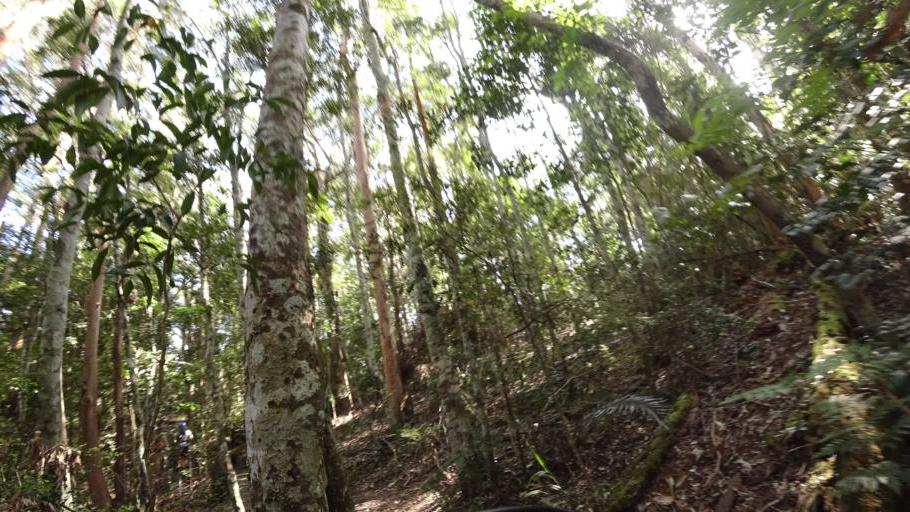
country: AU
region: Queensland
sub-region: Moreton Bay
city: Highvale
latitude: -27.3986
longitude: 152.7899
